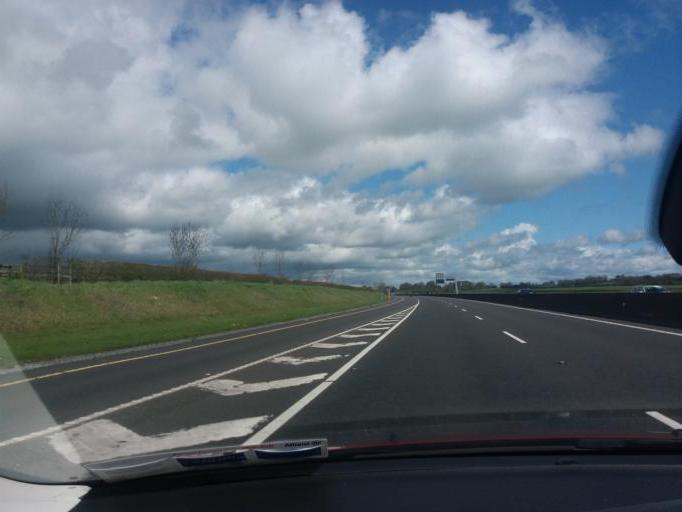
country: IE
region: Leinster
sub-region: Laois
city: Rathdowney
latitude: 52.7330
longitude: -7.5817
